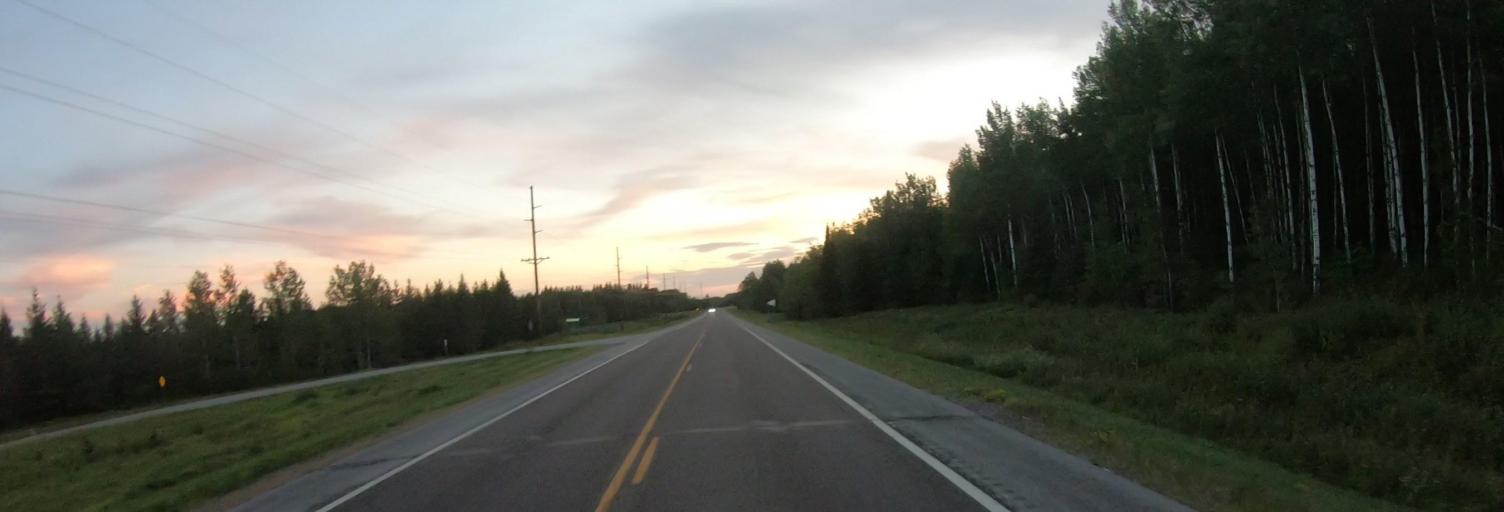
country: US
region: Minnesota
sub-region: Saint Louis County
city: Parkville
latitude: 47.8460
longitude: -92.5176
